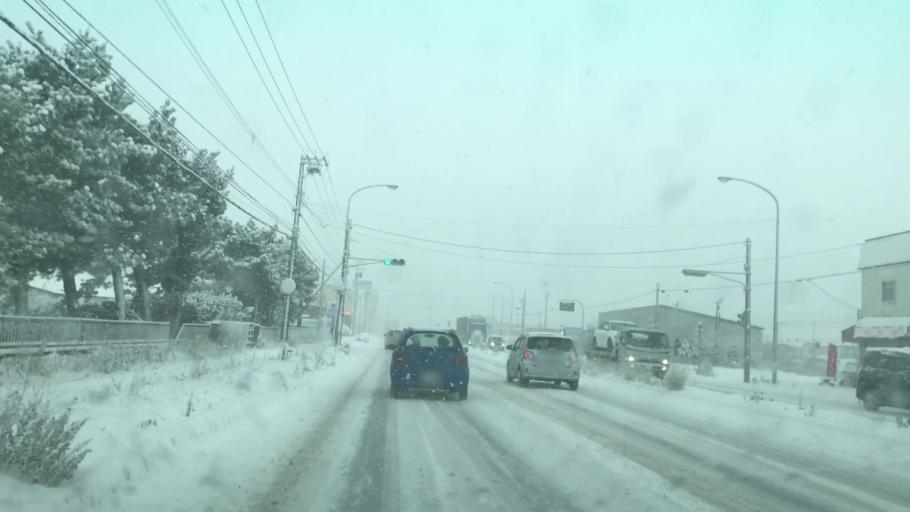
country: JP
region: Hokkaido
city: Muroran
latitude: 42.3847
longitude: 141.0772
